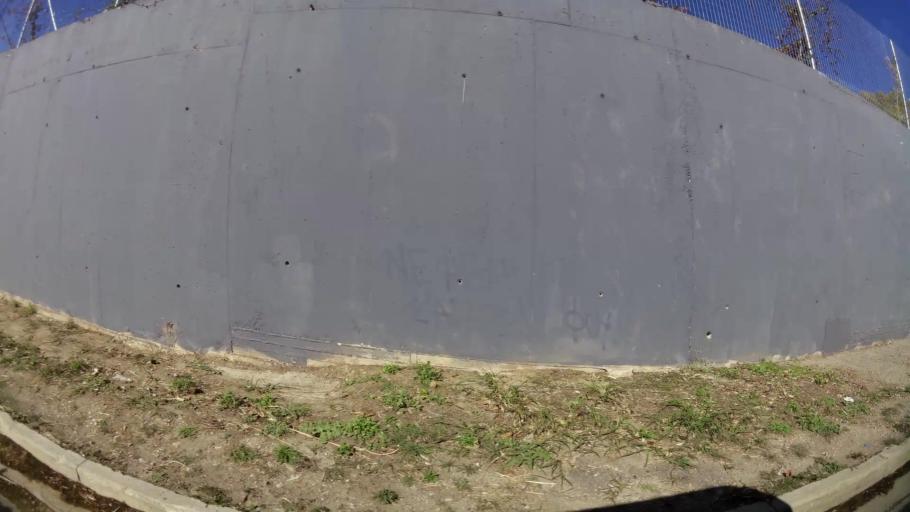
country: GR
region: Attica
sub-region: Nomarchia Anatolikis Attikis
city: Pikermi
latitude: 37.9980
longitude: 23.9238
